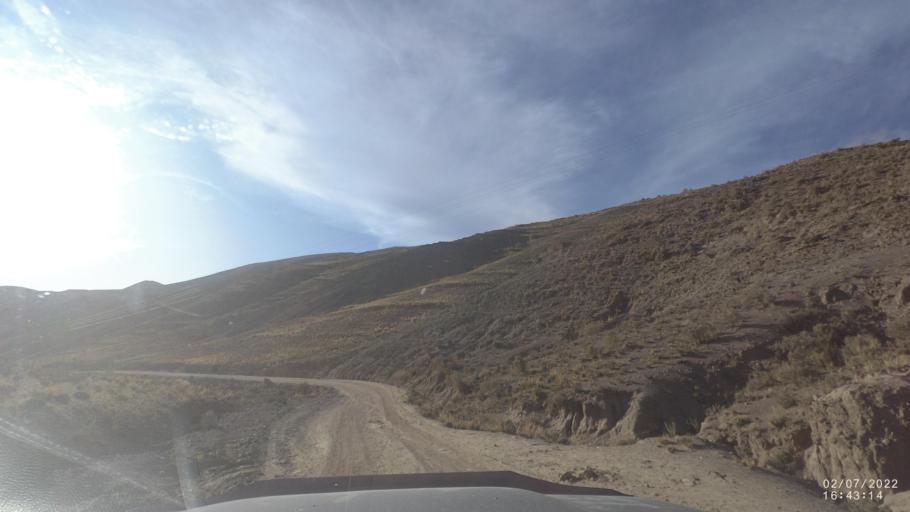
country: BO
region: Cochabamba
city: Irpa Irpa
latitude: -17.9736
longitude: -66.5048
